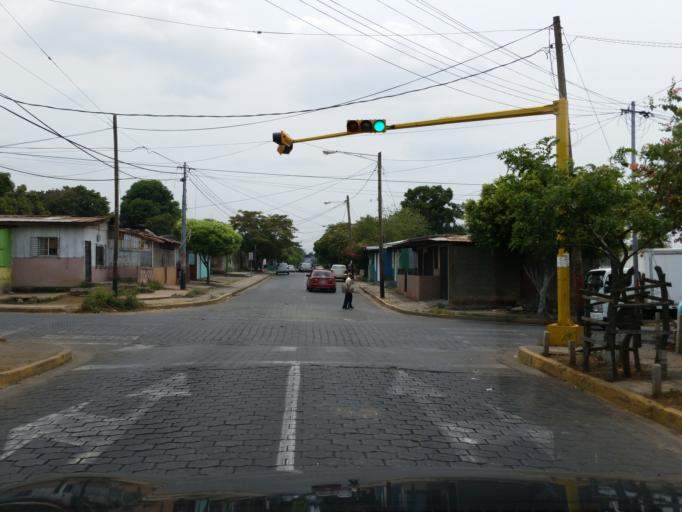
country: NI
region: Managua
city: Managua
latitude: 12.1276
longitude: -86.2512
